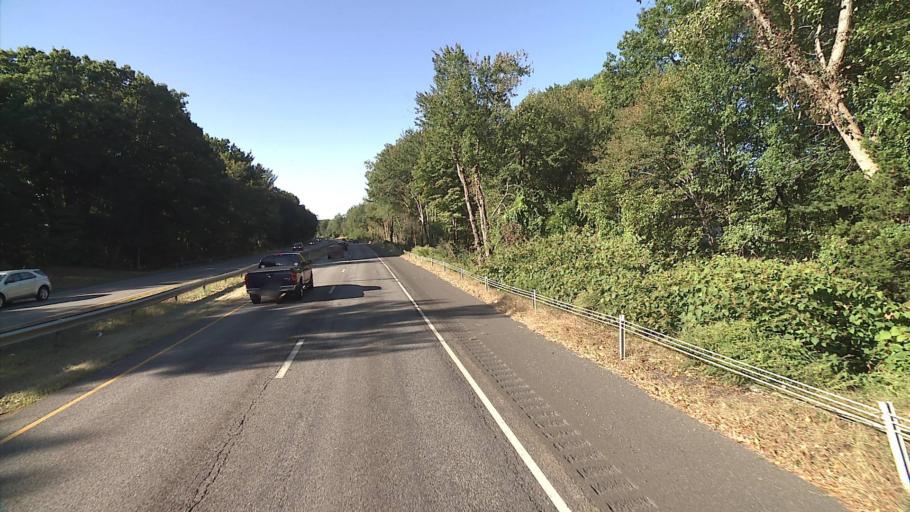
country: US
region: Connecticut
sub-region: New Haven County
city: Wallingford
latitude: 41.4870
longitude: -72.8158
